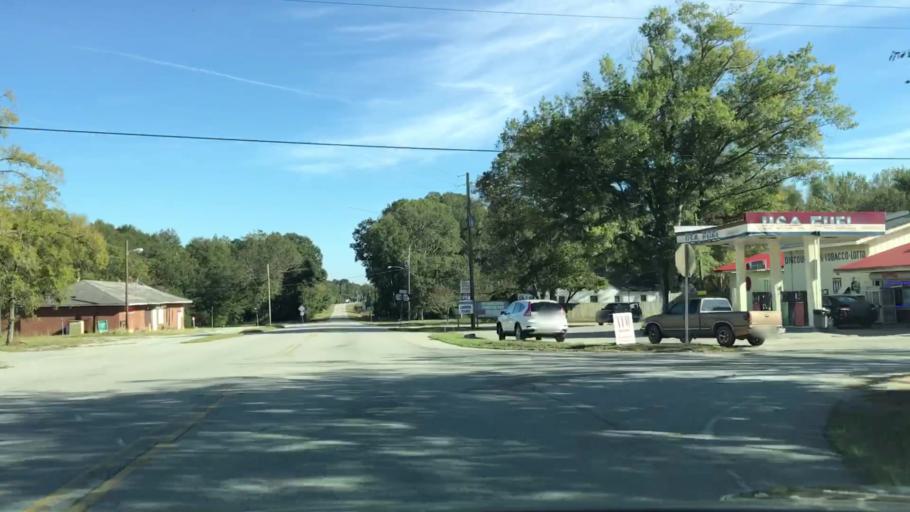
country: US
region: Georgia
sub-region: Warren County
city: Firing Range
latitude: 33.4622
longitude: -82.7072
